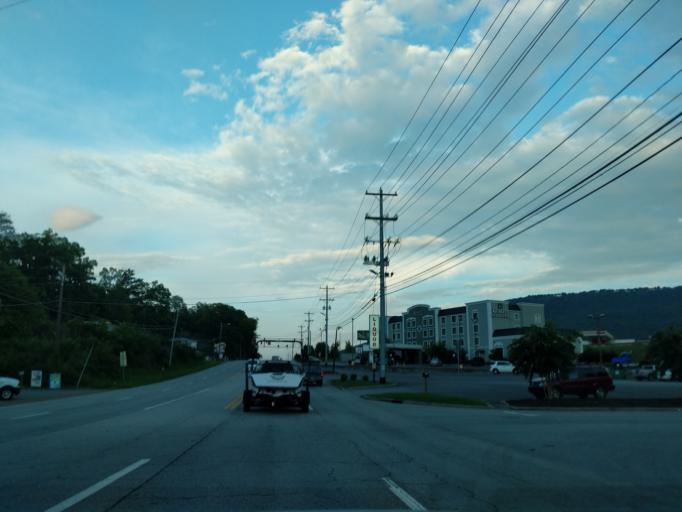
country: US
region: Tennessee
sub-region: Hamilton County
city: Lookout Mountain
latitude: 35.0183
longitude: -85.3779
